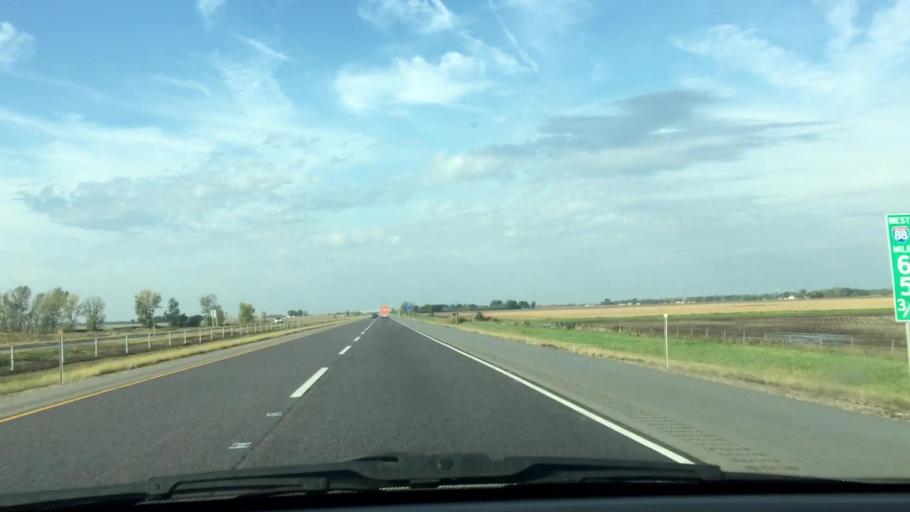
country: US
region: Illinois
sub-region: Lee County
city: Franklin Grove
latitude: 41.8432
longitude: -89.2533
